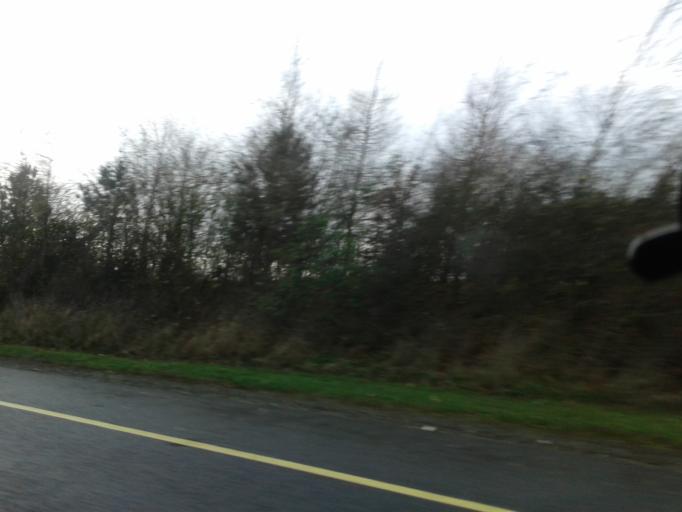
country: IE
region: Leinster
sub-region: An Mhi
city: Ashbourne
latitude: 53.4771
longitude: -6.3704
